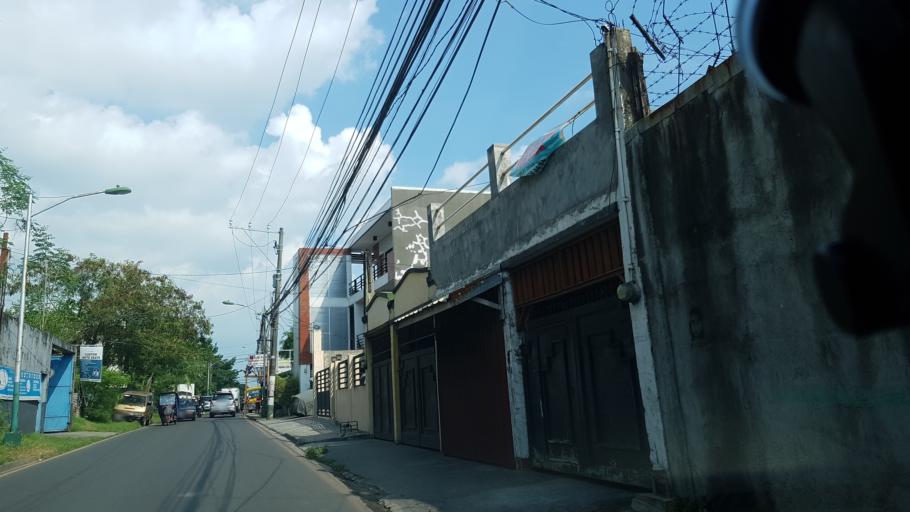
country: PH
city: Sambayanihan People's Village
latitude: 14.4785
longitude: 121.0285
